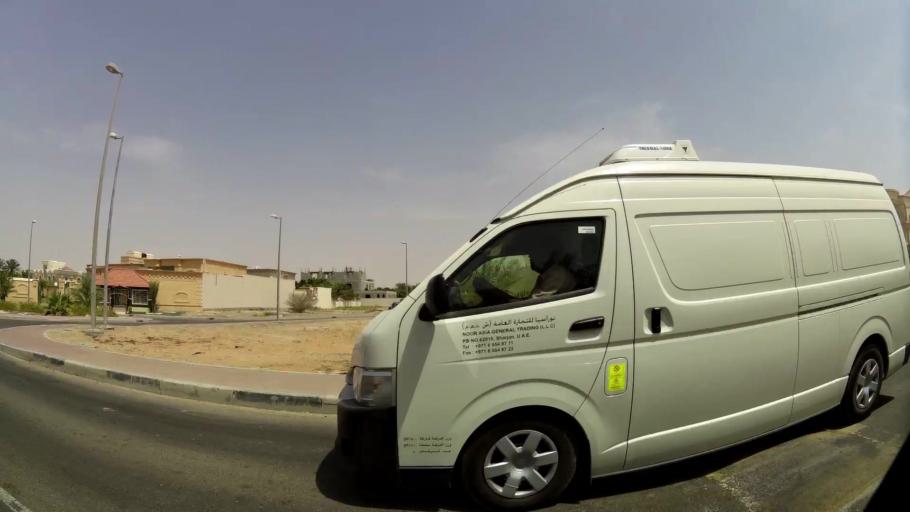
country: AE
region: Abu Dhabi
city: Al Ain
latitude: 24.1774
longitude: 55.7154
